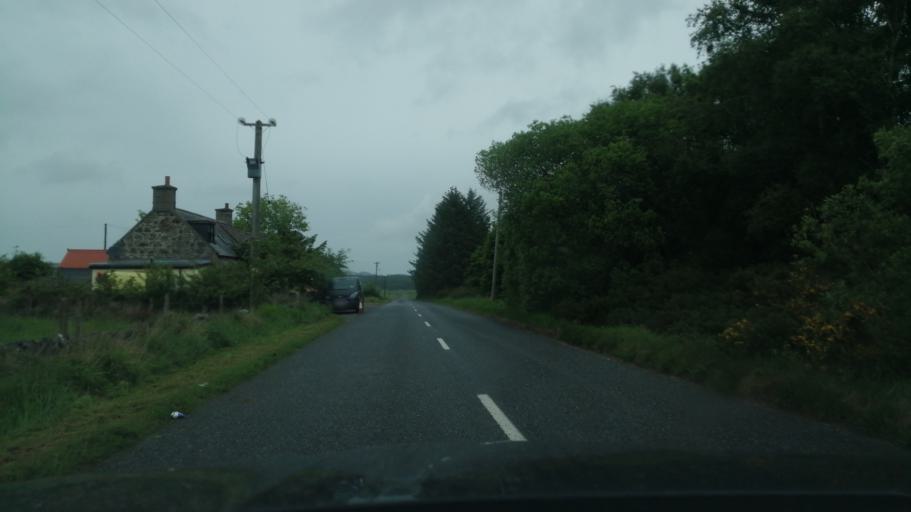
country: GB
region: Scotland
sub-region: Aberdeenshire
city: Portsoy
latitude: 57.6109
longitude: -2.7242
